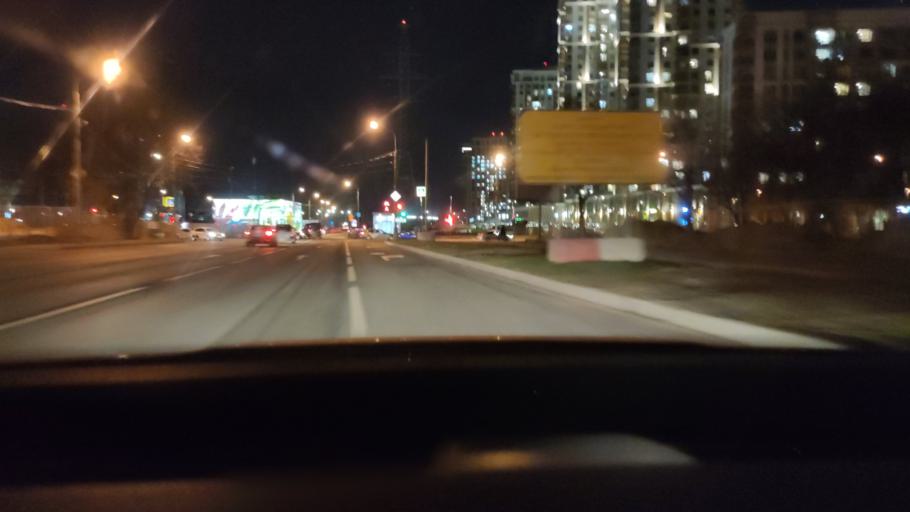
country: RU
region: Moscow
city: Sviblovo
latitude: 55.8468
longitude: 37.6413
